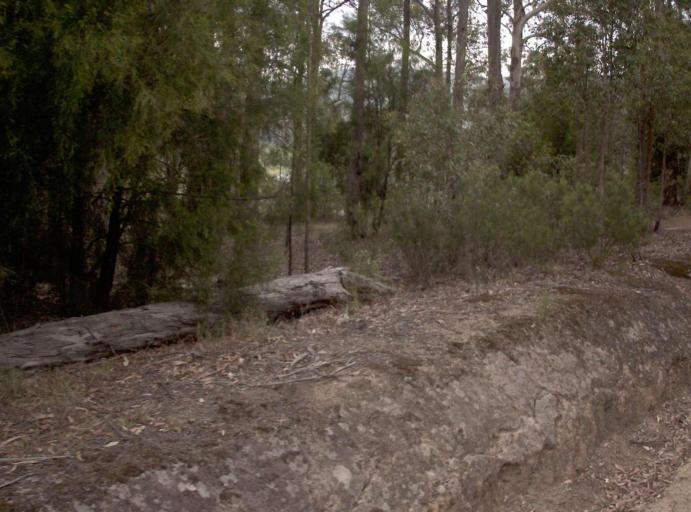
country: AU
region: New South Wales
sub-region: Bombala
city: Bombala
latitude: -37.4882
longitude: 149.1821
